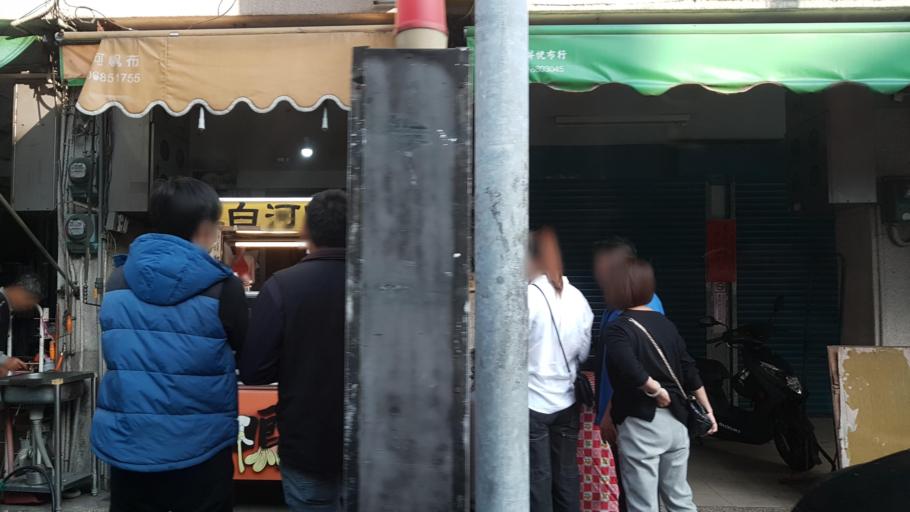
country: TW
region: Taiwan
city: Xinying
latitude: 23.3492
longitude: 120.4149
